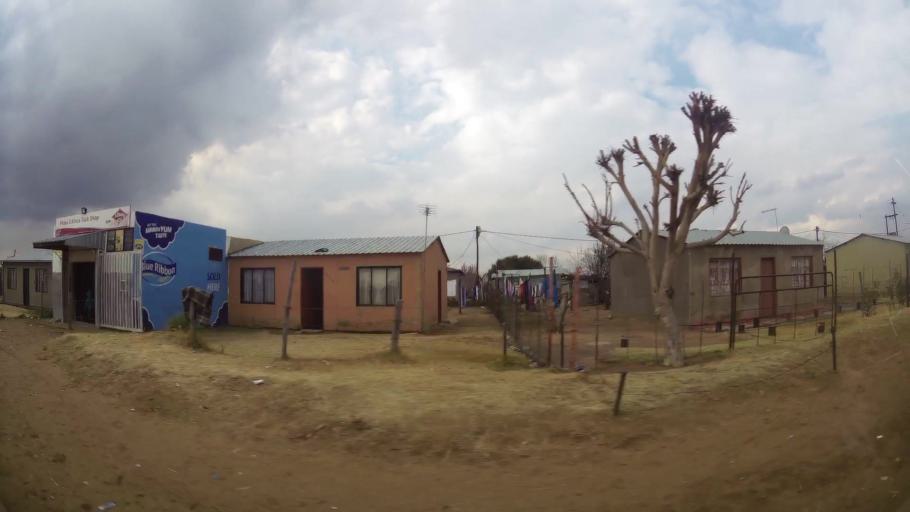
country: ZA
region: Orange Free State
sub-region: Fezile Dabi District Municipality
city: Sasolburg
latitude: -26.8640
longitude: 27.8657
